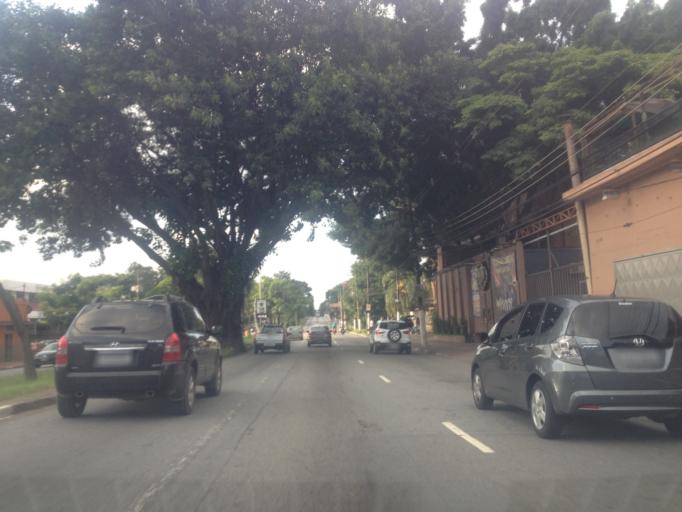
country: BR
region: Sao Paulo
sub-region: Diadema
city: Diadema
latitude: -23.6999
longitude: -46.7150
